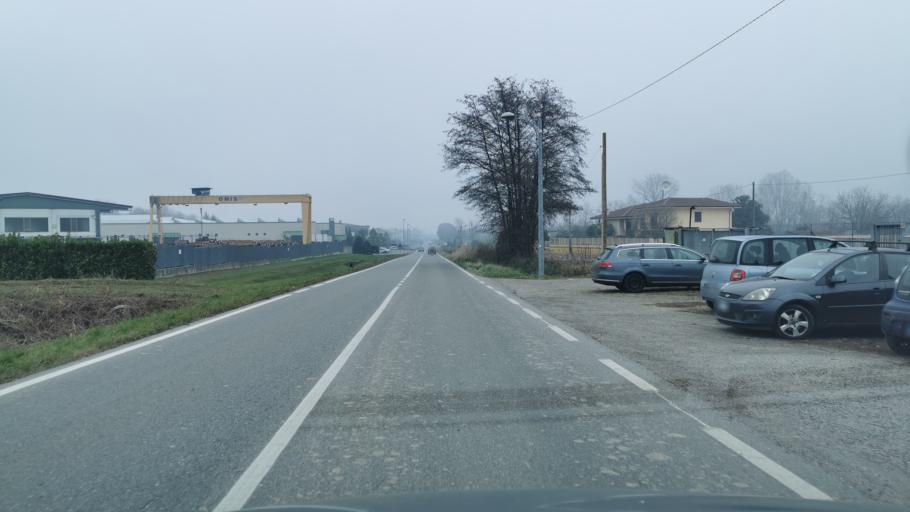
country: IT
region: Piedmont
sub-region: Provincia di Torino
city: Rivara
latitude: 45.3274
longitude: 7.6488
